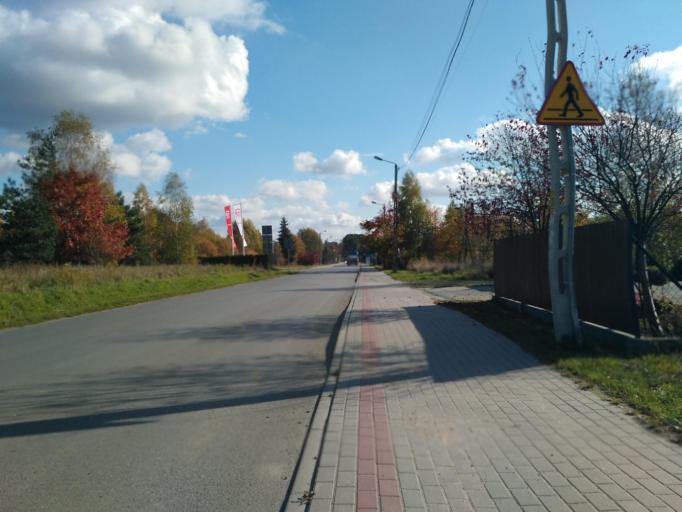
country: PL
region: Subcarpathian Voivodeship
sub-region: Powiat rzeszowski
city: Glogow Malopolski
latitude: 50.1515
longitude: 21.9471
